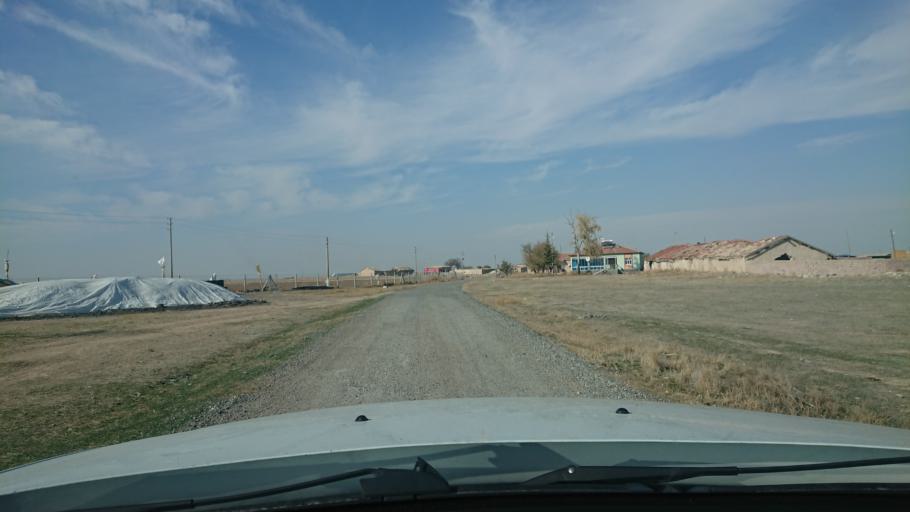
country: TR
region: Aksaray
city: Sultanhani
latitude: 38.2565
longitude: 33.4777
